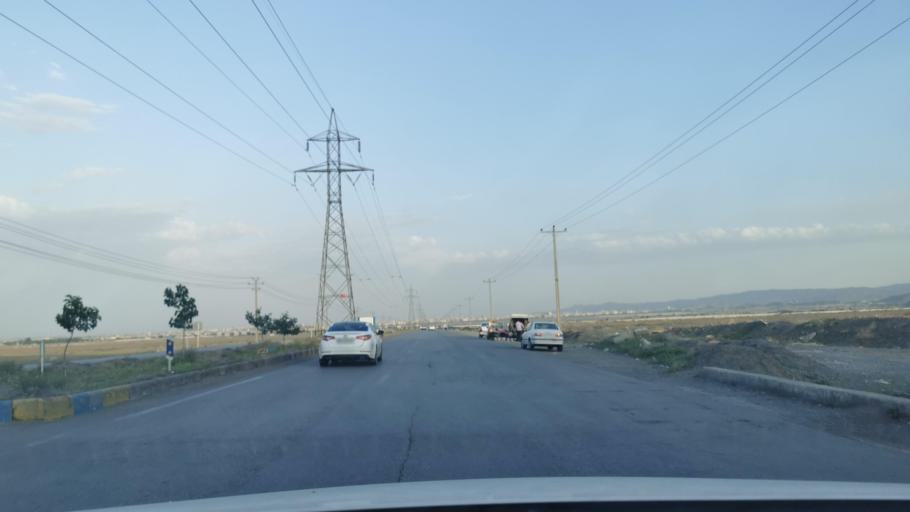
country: IR
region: Razavi Khorasan
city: Torqabeh
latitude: 36.4220
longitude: 59.4271
